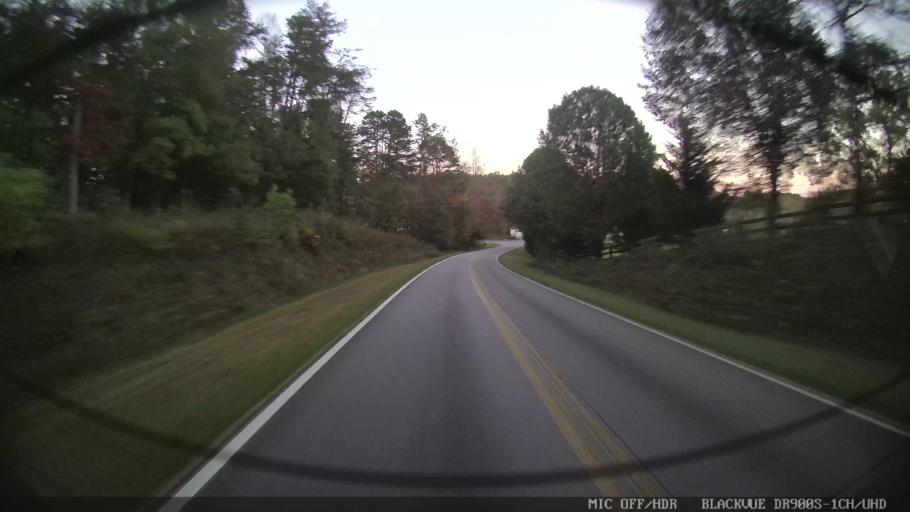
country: US
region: North Carolina
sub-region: Clay County
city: Hayesville
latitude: 34.9697
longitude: -83.8807
